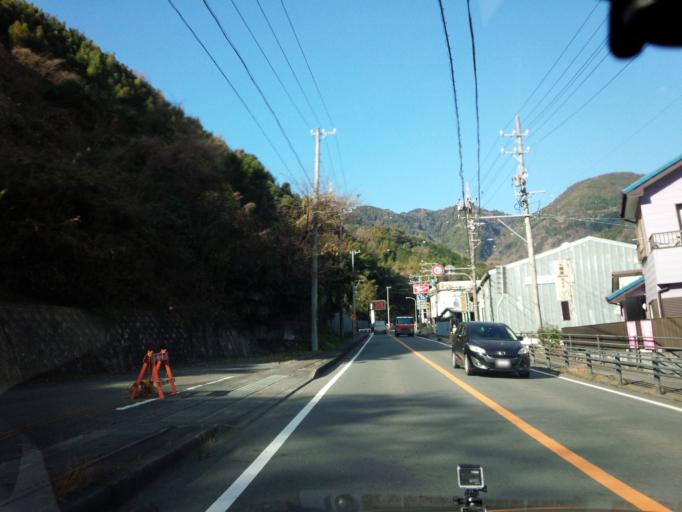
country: JP
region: Shizuoka
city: Shizuoka-shi
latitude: 35.0796
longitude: 138.5169
